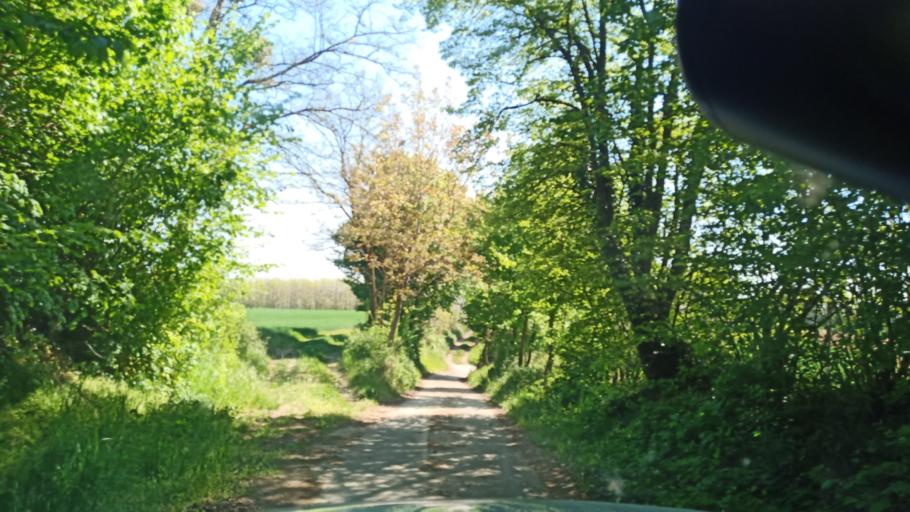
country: HU
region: Zala
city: Heviz
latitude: 46.7772
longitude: 17.0942
